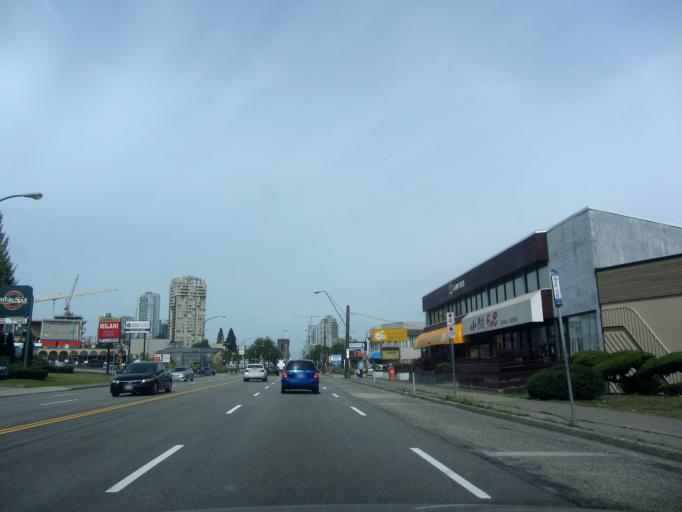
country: CA
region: British Columbia
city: Burnaby
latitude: 49.2186
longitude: -122.9622
